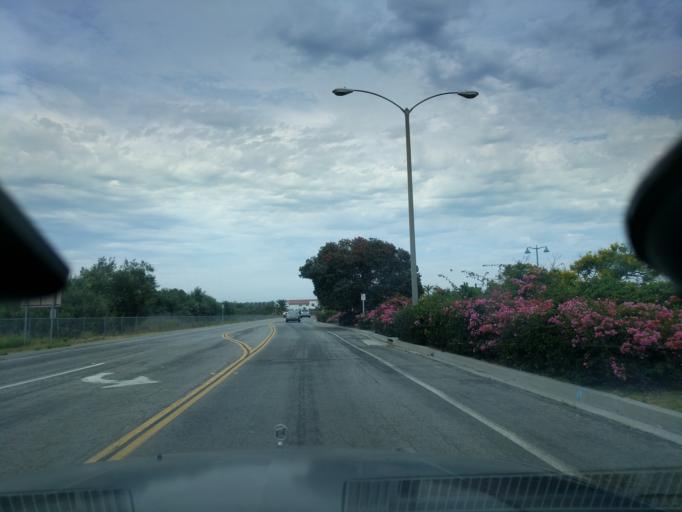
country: US
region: California
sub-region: Santa Barbara County
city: Goleta
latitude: 34.4262
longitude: -119.8319
